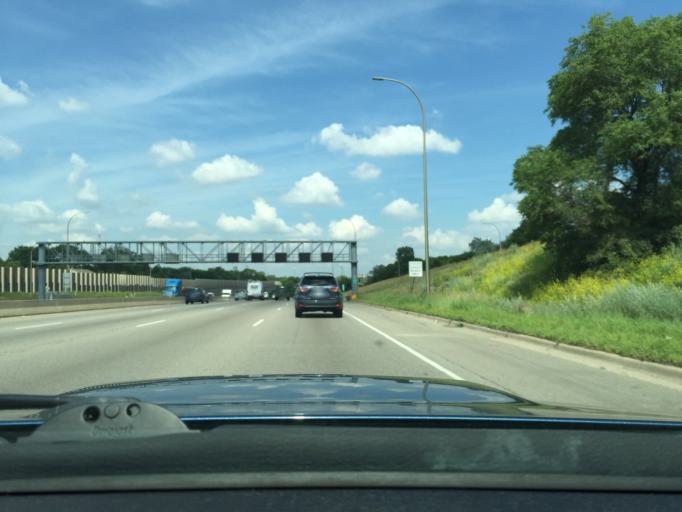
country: US
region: Minnesota
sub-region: Ramsey County
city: Lauderdale
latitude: 44.9566
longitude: -93.1932
